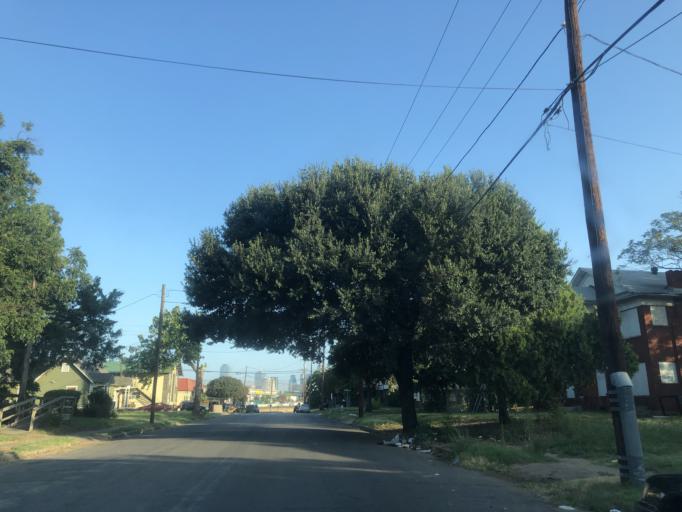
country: US
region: Texas
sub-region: Dallas County
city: Dallas
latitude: 32.7570
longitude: -96.7712
